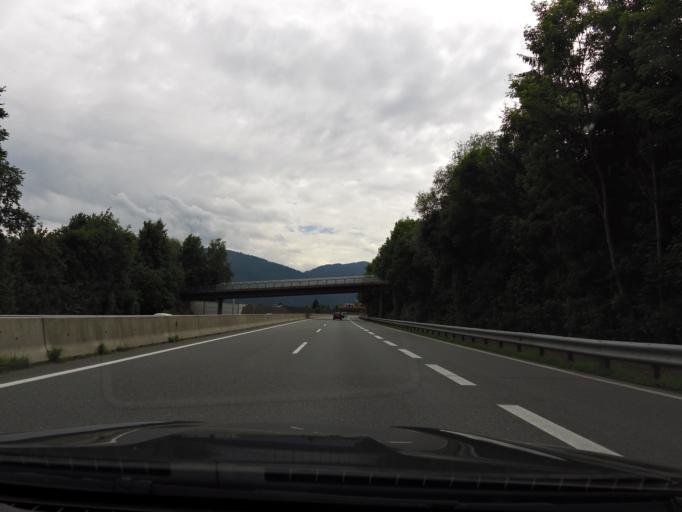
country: AT
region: Tyrol
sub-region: Politischer Bezirk Kufstein
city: Angath
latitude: 47.5143
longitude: 12.0647
